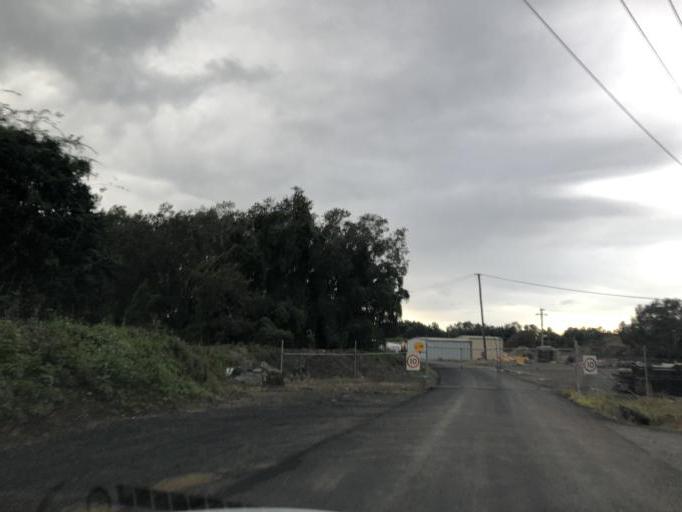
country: AU
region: New South Wales
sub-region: Coffs Harbour
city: Coffs Harbour
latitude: -30.3112
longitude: 153.1334
